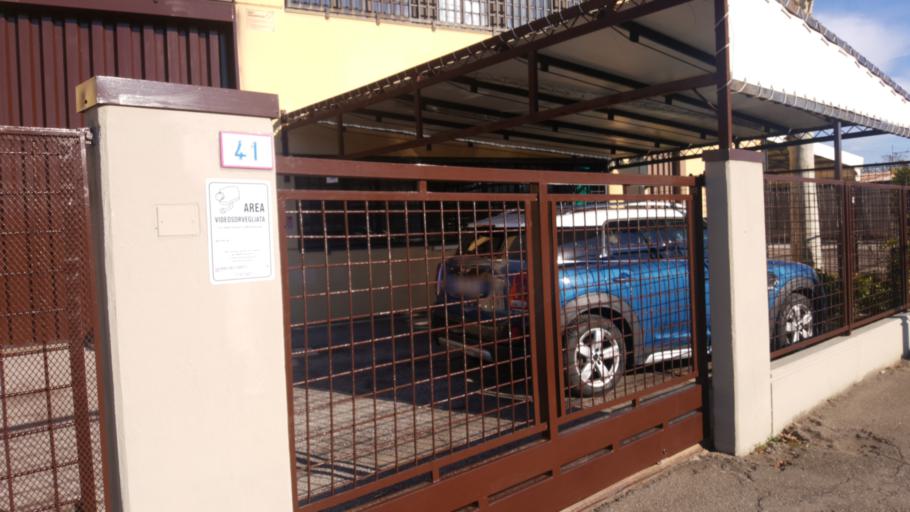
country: IT
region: Emilia-Romagna
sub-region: Provincia di Bologna
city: Calderara di Reno
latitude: 44.5469
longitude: 11.2845
